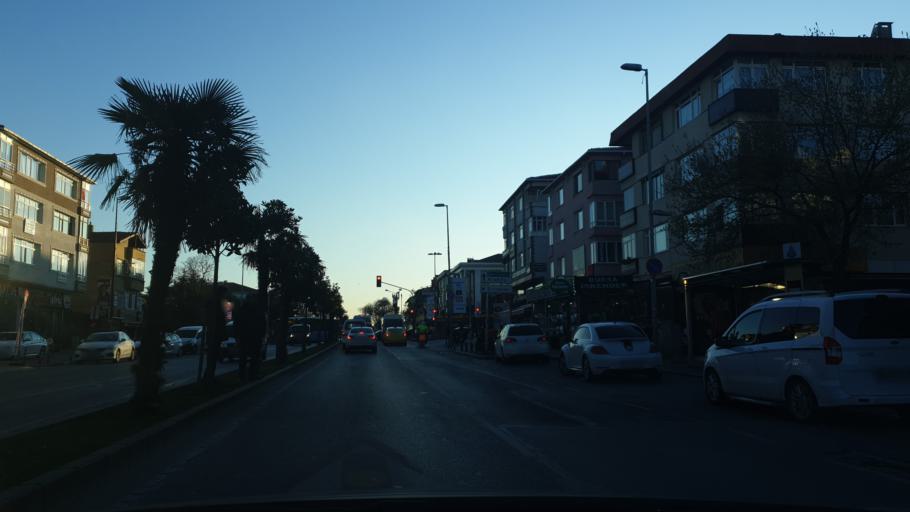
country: TR
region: Istanbul
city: Bahcelievler
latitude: 41.0012
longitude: 28.8621
